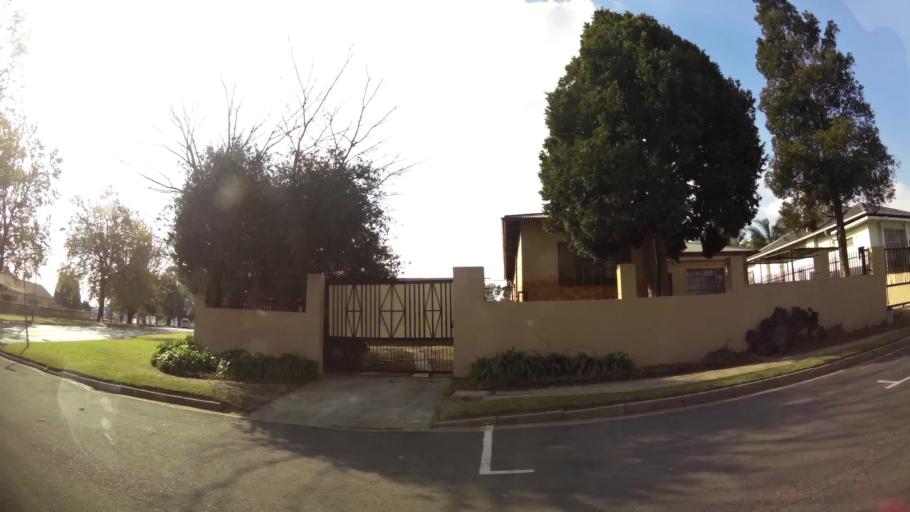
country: ZA
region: Gauteng
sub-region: West Rand District Municipality
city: Krugersdorp
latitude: -26.1005
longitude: 27.7653
